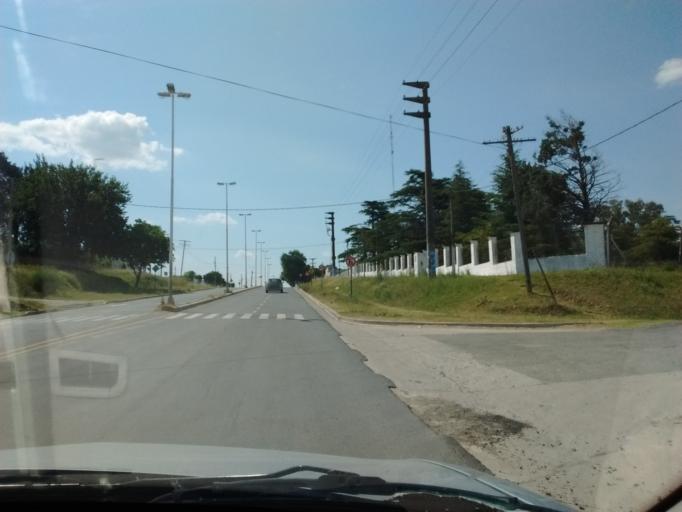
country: AR
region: Entre Rios
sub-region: Departamento de Victoria
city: Victoria
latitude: -32.6143
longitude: -60.1391
